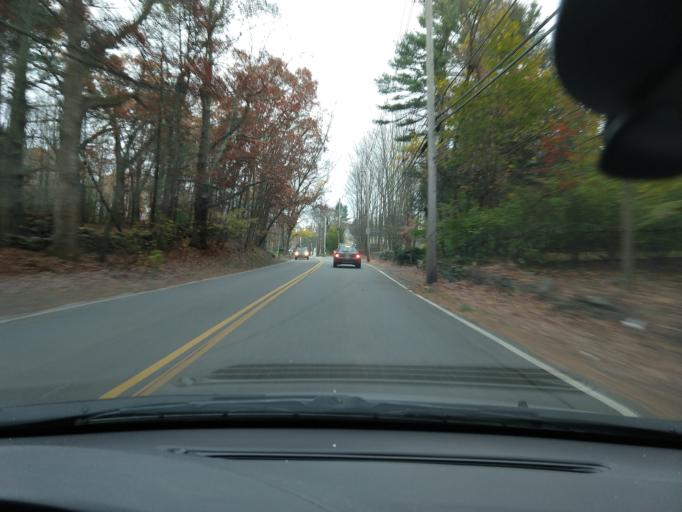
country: US
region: Massachusetts
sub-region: Middlesex County
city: Carlisle
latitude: 42.5329
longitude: -71.3482
